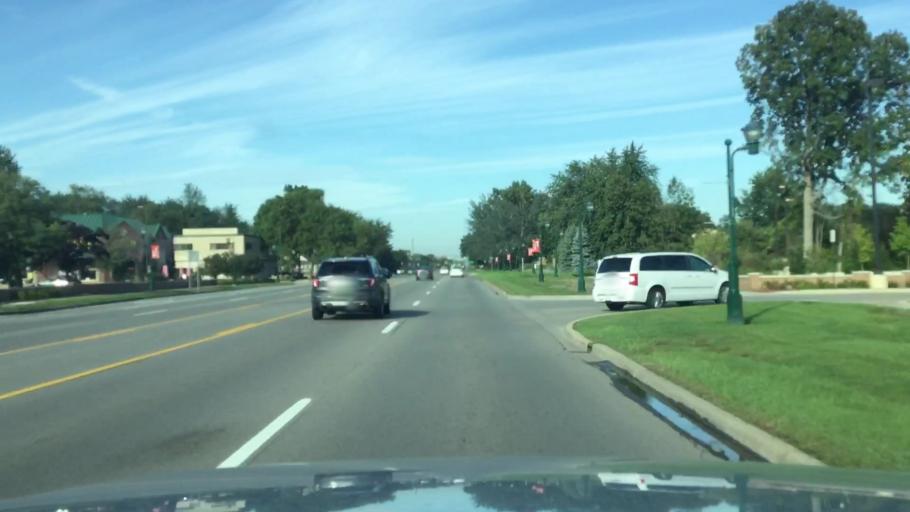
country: US
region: Michigan
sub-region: Wayne County
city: Canton
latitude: 42.3225
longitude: -83.4625
